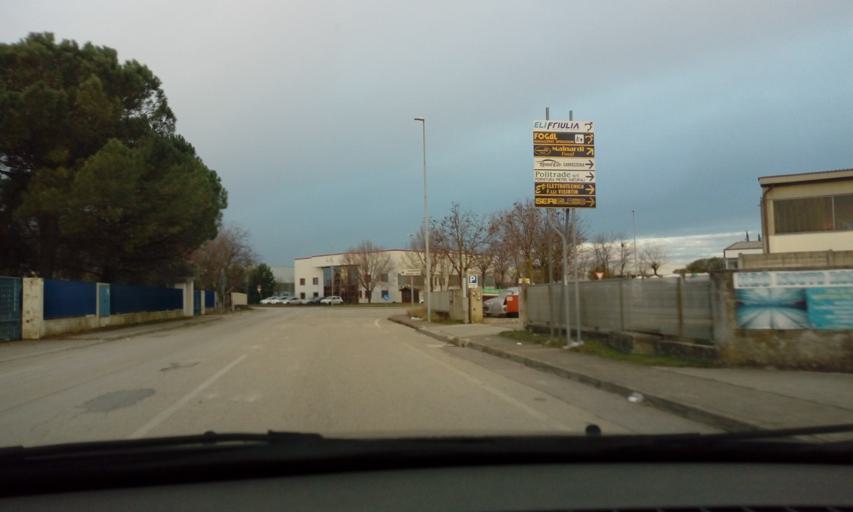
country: IT
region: Friuli Venezia Giulia
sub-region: Provincia di Gorizia
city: Begliano
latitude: 45.8220
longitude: 13.4759
